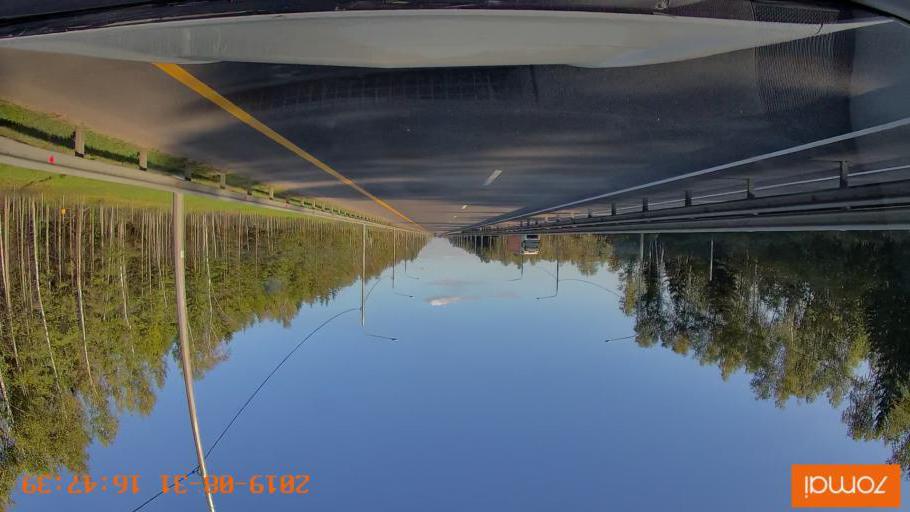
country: RU
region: Kaluga
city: Pyatovskiy
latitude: 54.6580
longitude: 36.1406
